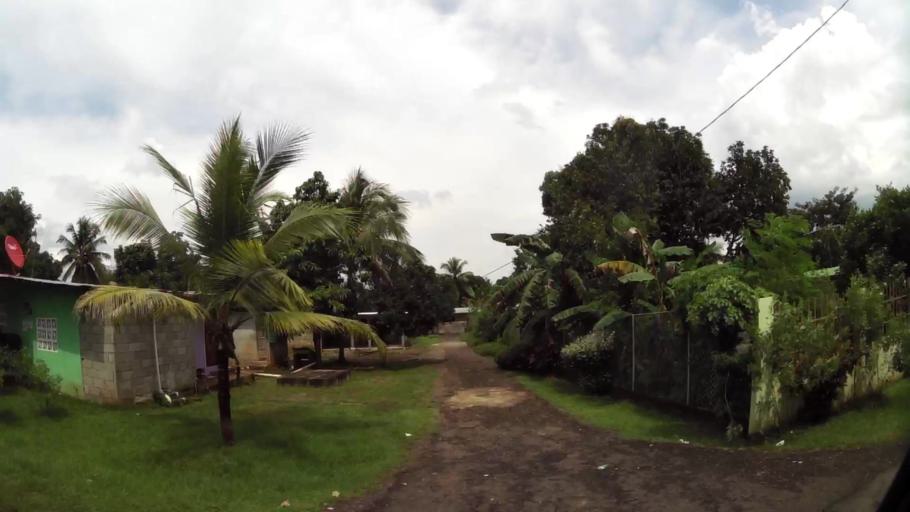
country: PA
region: Panama
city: Cabra Numero Uno
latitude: 9.1098
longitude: -79.3272
